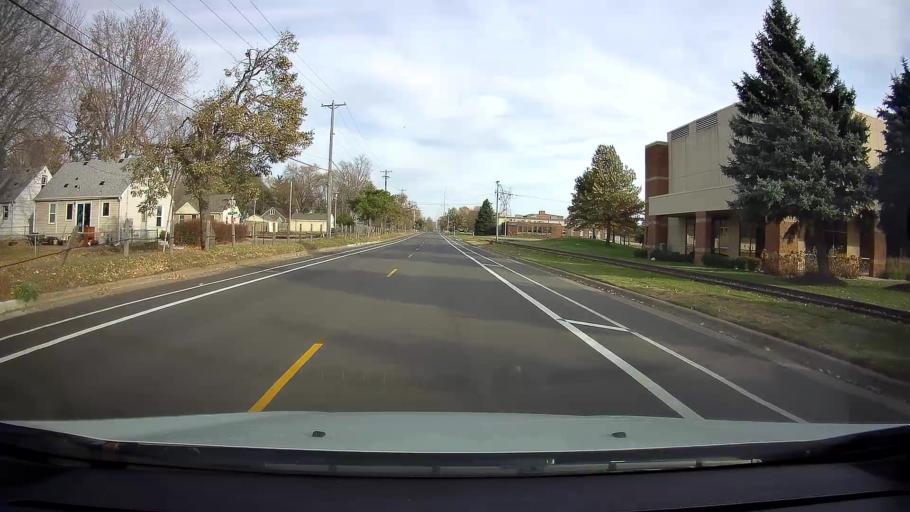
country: US
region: Minnesota
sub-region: Ramsey County
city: Lauderdale
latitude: 44.9842
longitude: -93.2249
